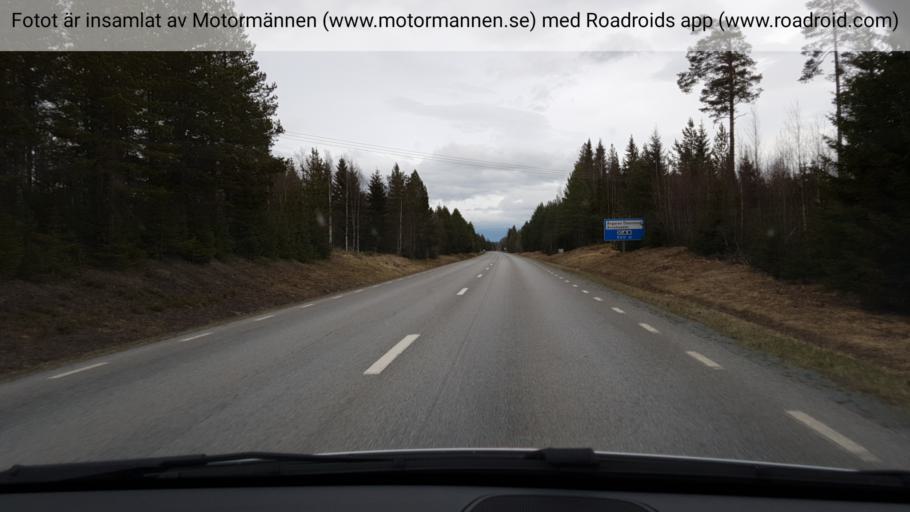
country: SE
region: Jaemtland
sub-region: Krokoms Kommun
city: Valla
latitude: 63.2610
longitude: 13.9771
